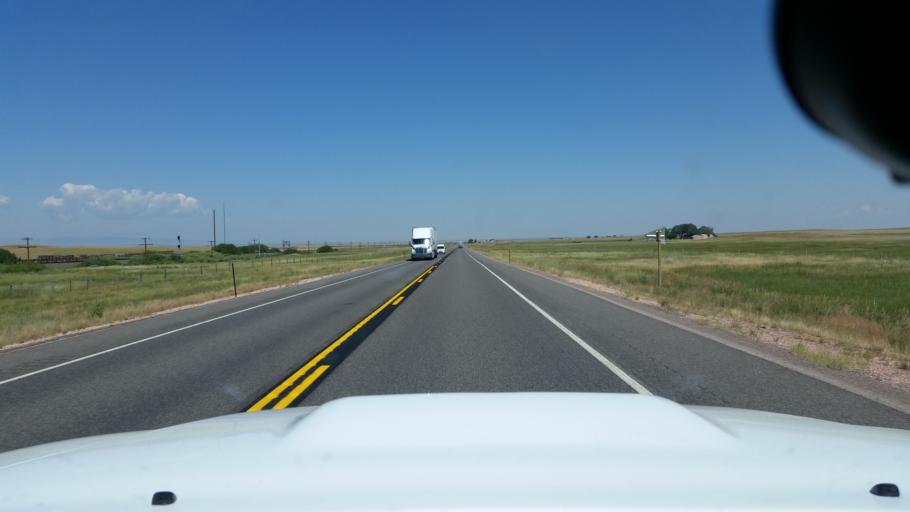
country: US
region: Wyoming
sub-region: Albany County
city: Laramie
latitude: 41.1634
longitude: -105.5799
